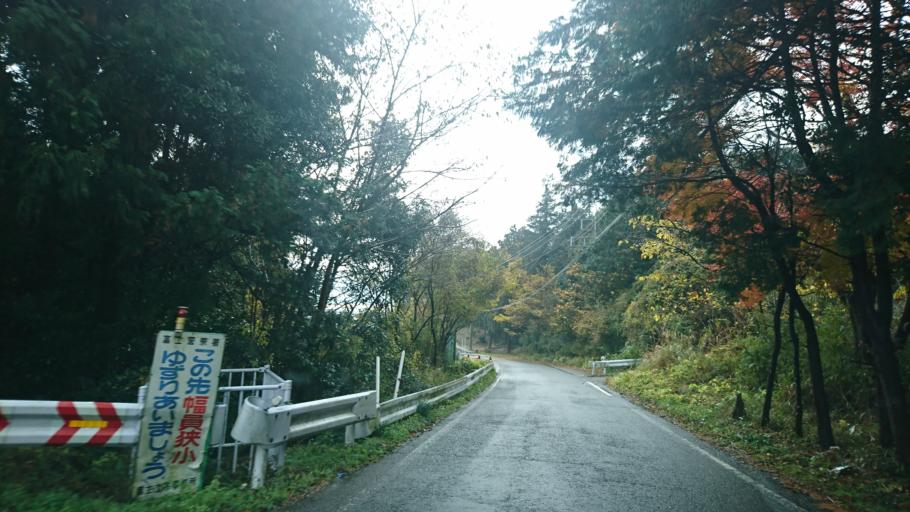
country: JP
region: Shizuoka
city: Fuji
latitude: 35.1794
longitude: 138.7263
